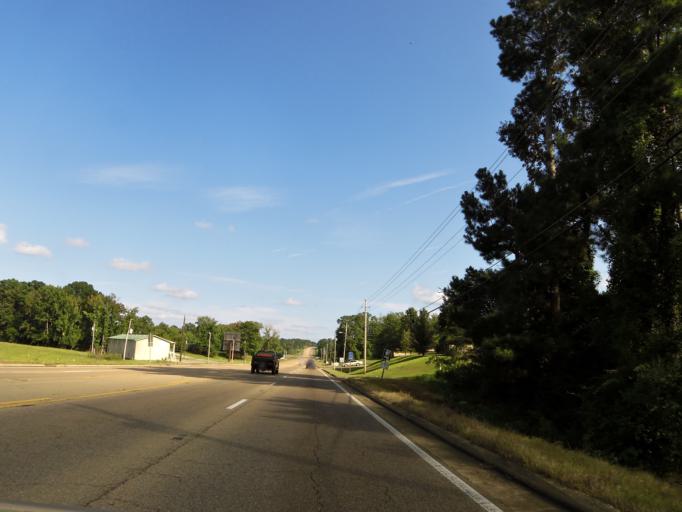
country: US
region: Mississippi
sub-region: Alcorn County
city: Farmington
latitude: 34.9048
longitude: -88.4844
